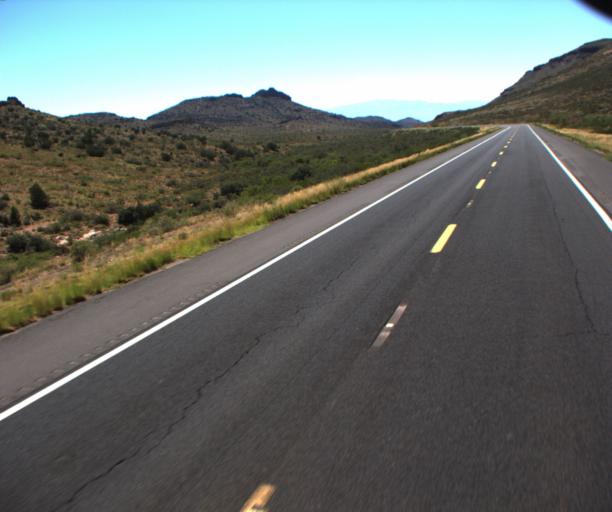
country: US
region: Arizona
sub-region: Greenlee County
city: Clifton
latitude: 32.8516
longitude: -109.3300
